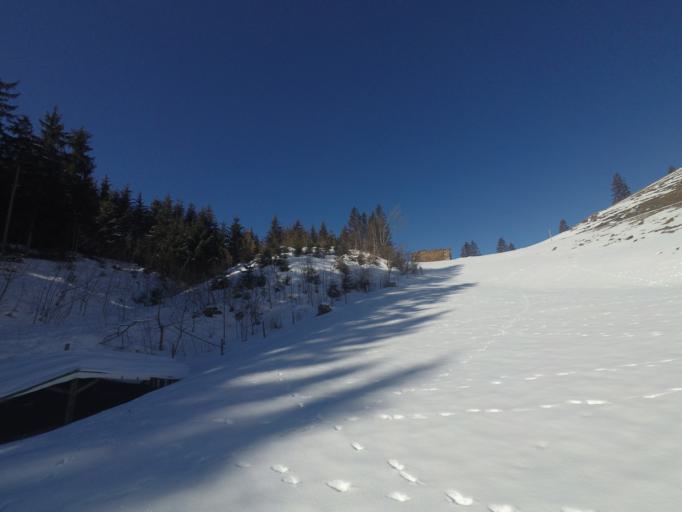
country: AT
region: Salzburg
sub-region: Politischer Bezirk Zell am See
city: Lend
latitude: 47.3211
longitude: 13.0380
